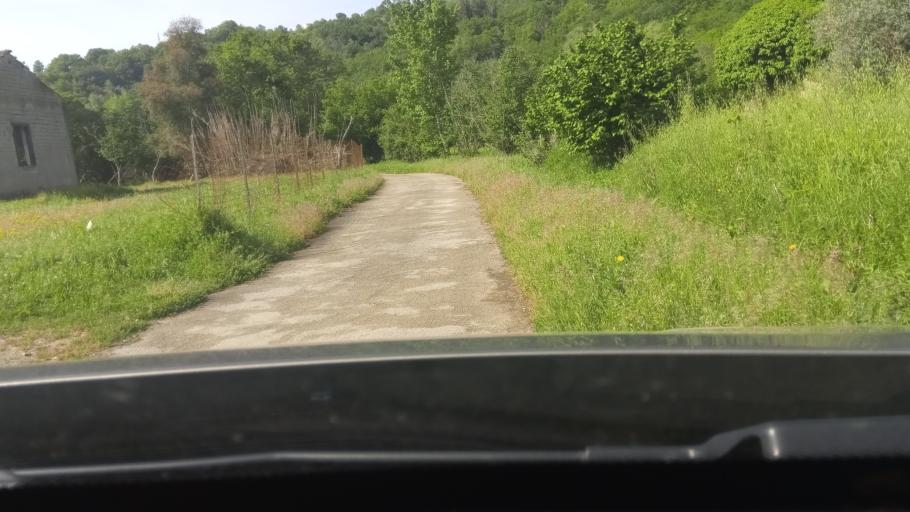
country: IT
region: Latium
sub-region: Provincia di Latina
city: Minturno
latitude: 41.2791
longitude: 13.7663
